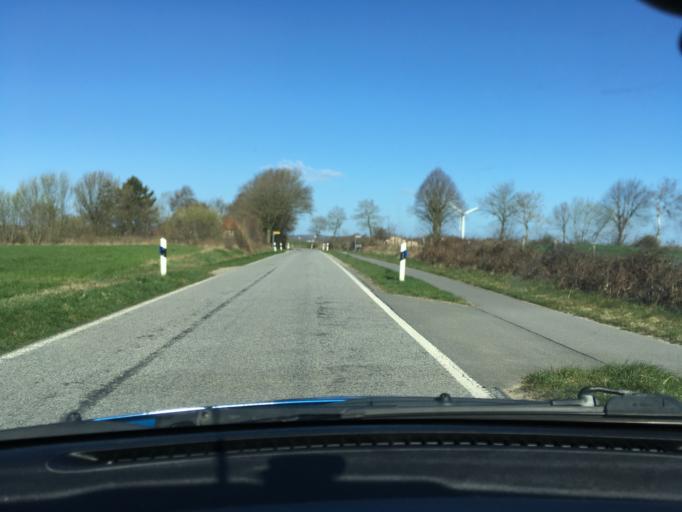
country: DE
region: Schleswig-Holstein
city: Borgwedel
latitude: 54.4978
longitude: 9.6495
